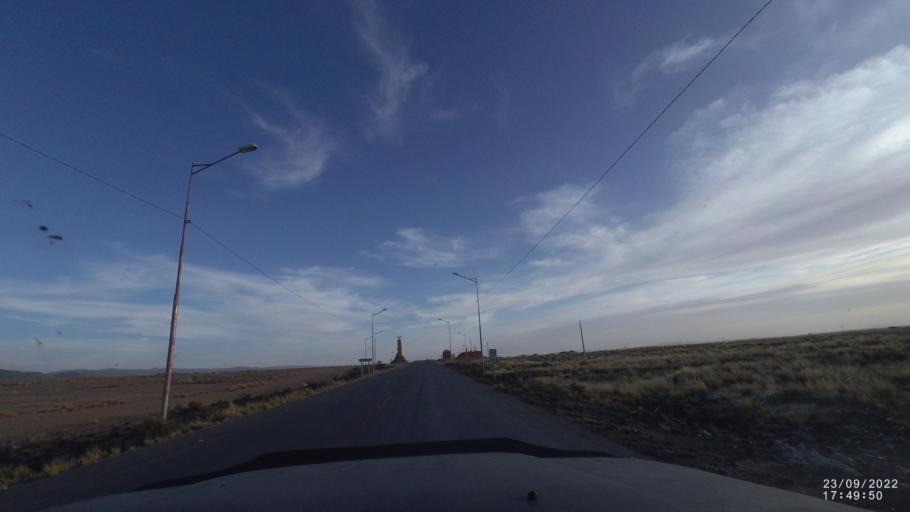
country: BO
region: Oruro
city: Challapata
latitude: -19.0246
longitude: -66.7770
